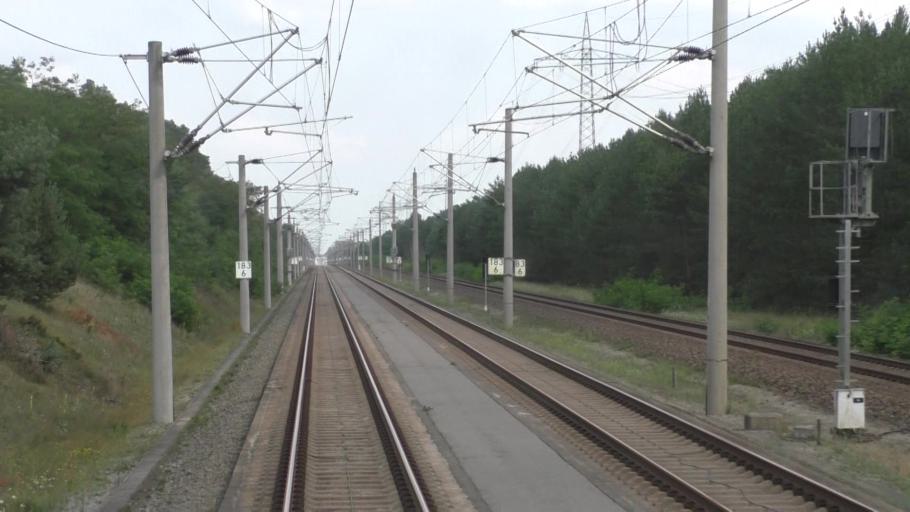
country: DE
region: Saxony-Anhalt
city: Schollene
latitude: 52.5904
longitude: 12.1675
